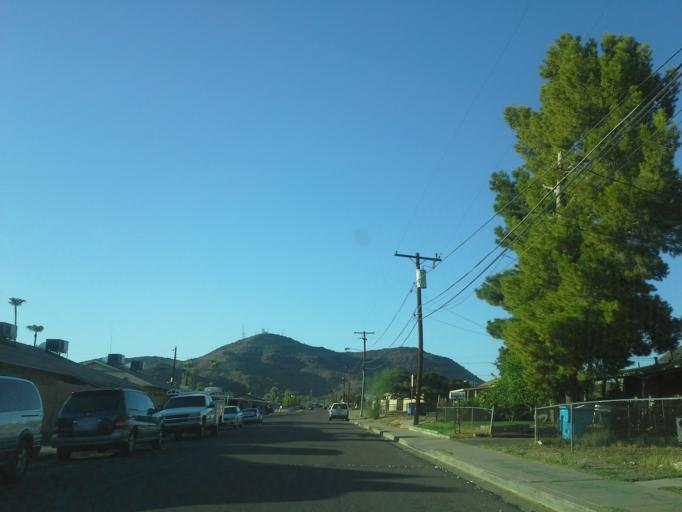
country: US
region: Arizona
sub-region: Maricopa County
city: Glendale
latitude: 33.5750
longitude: -112.0847
